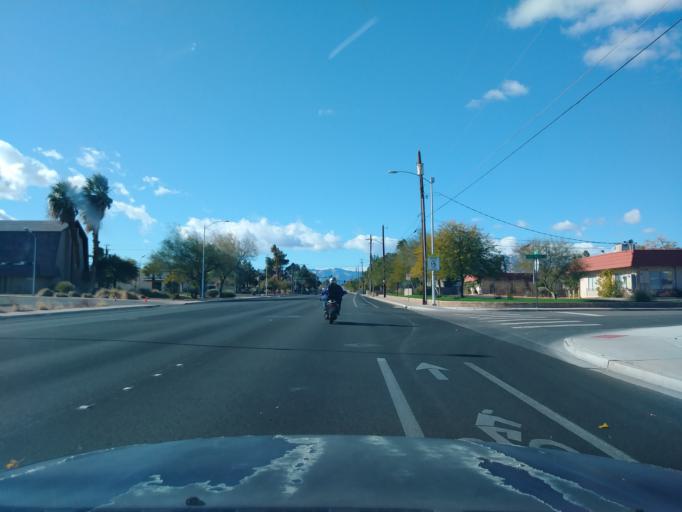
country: US
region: Nevada
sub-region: Clark County
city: Spring Valley
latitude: 36.1519
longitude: -115.2231
